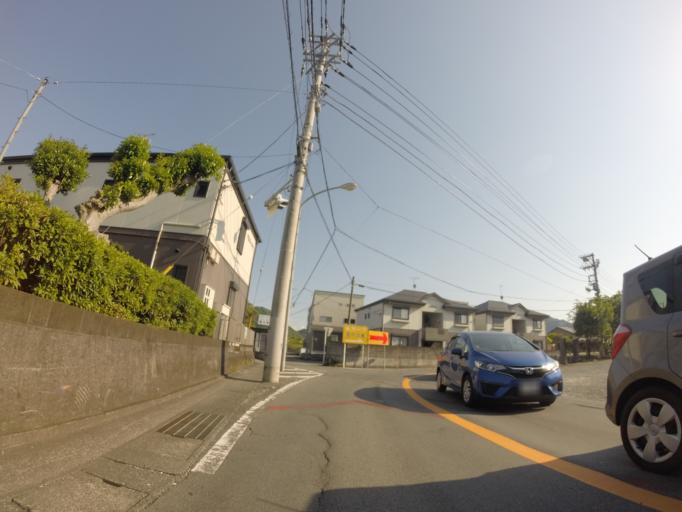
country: JP
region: Shizuoka
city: Mishima
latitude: 35.0773
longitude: 138.9219
